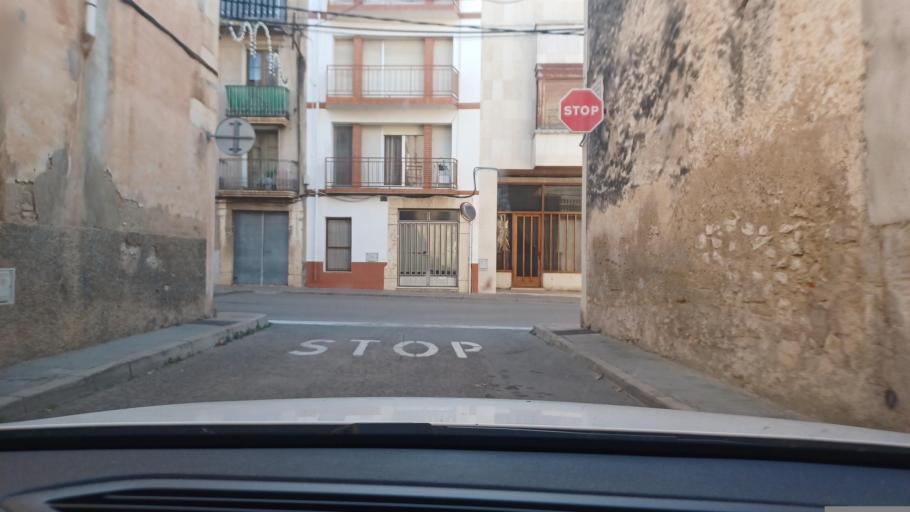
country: ES
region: Catalonia
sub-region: Provincia de Tarragona
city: Ulldecona
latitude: 40.5949
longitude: 0.4447
